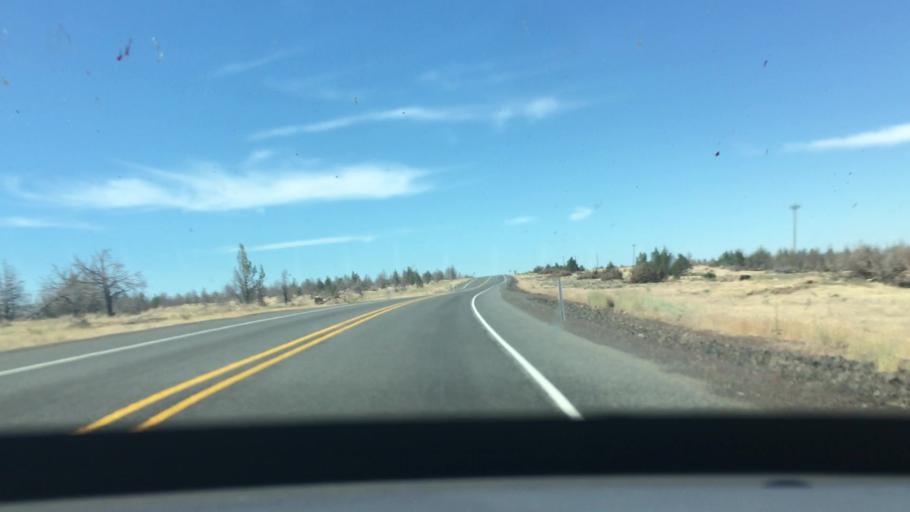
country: US
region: Oregon
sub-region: Jefferson County
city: Madras
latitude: 44.8977
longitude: -120.9367
